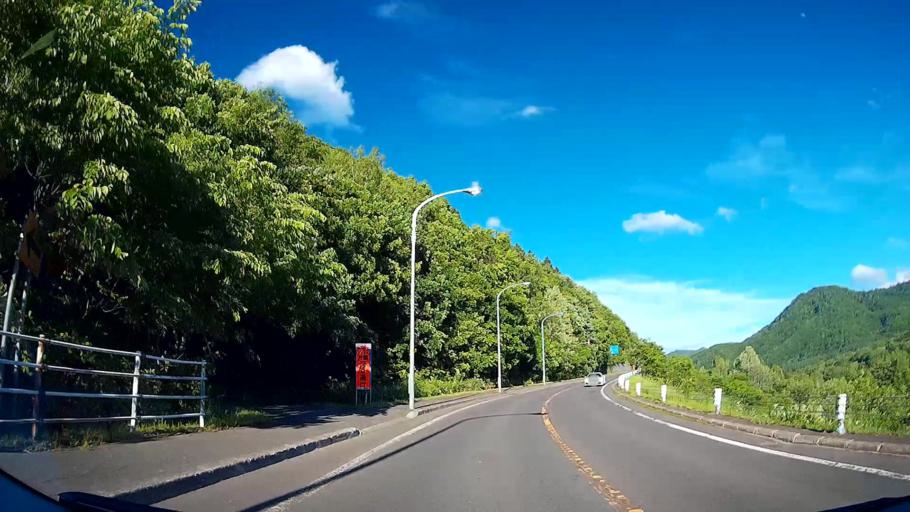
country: JP
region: Hokkaido
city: Sapporo
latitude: 42.9786
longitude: 141.1373
